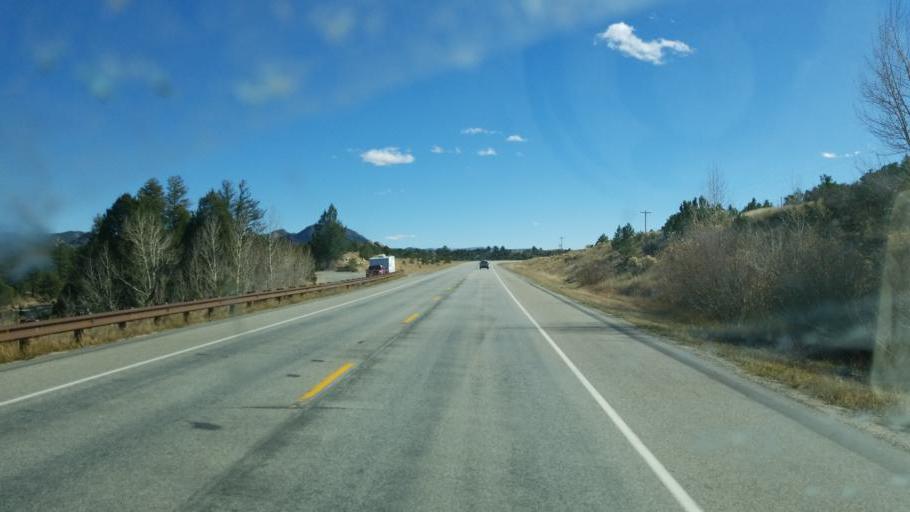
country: US
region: Colorado
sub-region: Chaffee County
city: Buena Vista
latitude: 38.8907
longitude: -106.1700
